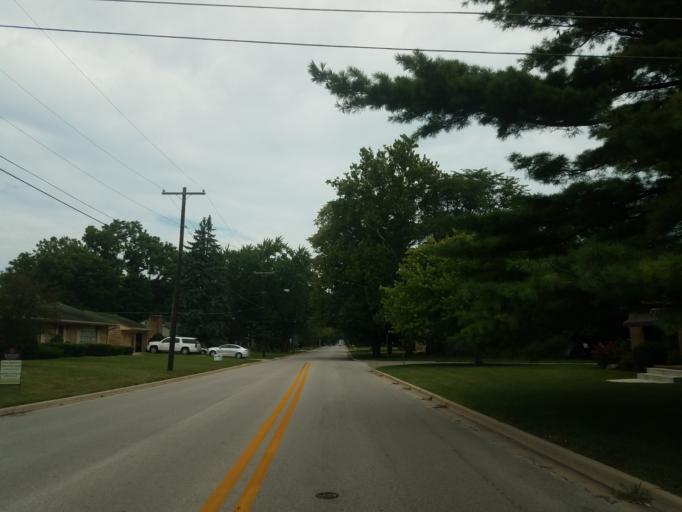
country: US
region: Illinois
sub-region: McLean County
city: Bloomington
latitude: 40.4742
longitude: -88.9628
